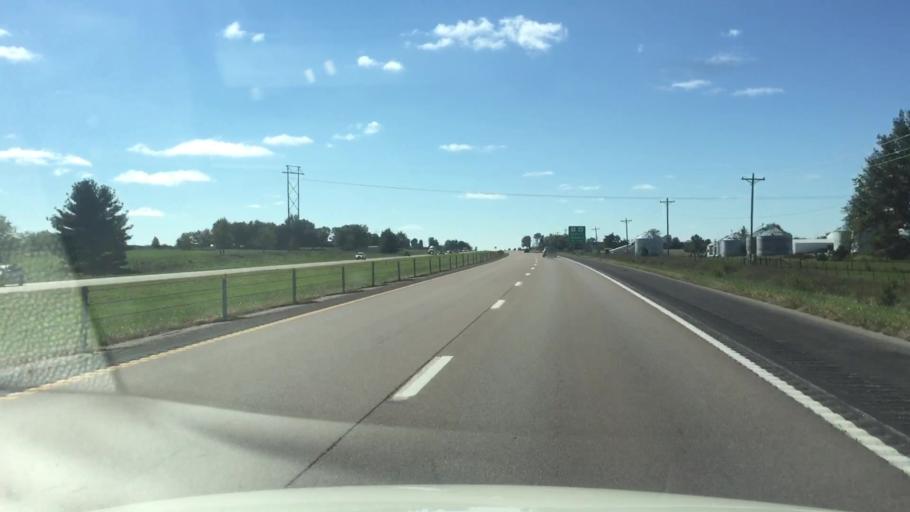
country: US
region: Missouri
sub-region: Boone County
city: Ashland
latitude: 38.7935
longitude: -92.2521
